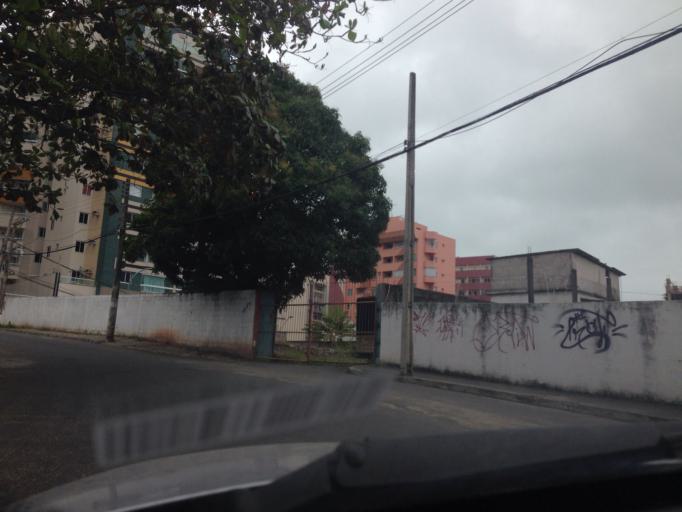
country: BR
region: Espirito Santo
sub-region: Guarapari
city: Guarapari
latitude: -20.6690
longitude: -40.4981
